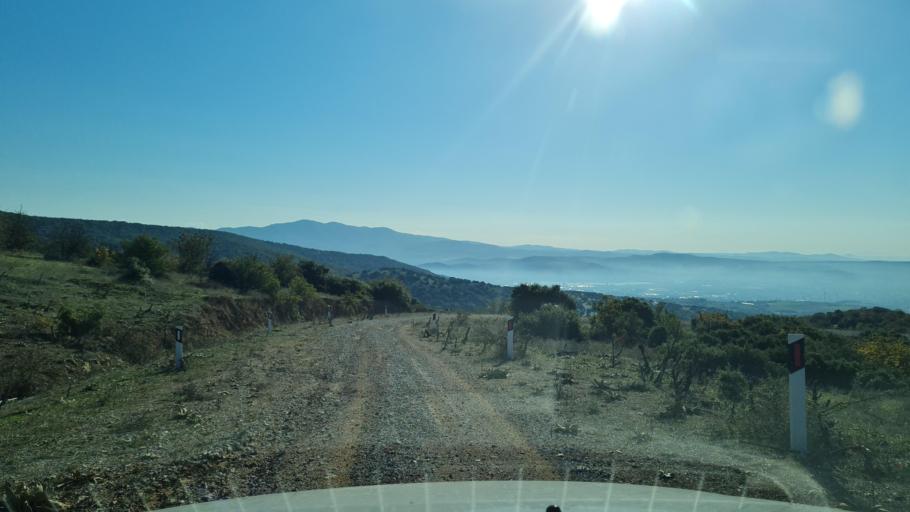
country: MK
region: Bogdanci
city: Bogdanci
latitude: 41.2189
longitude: 22.5474
